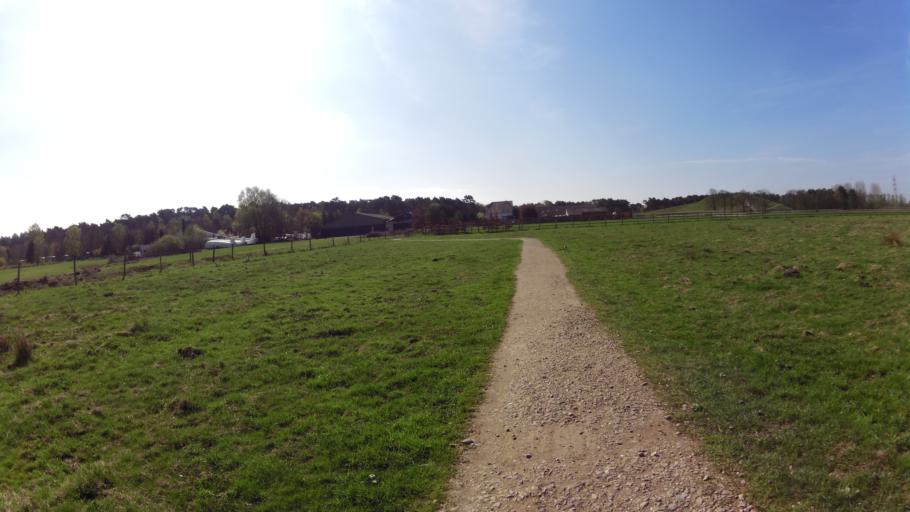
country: DE
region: North Rhine-Westphalia
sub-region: Regierungsbezirk Koln
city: Gangelt
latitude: 50.9798
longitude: 5.9936
